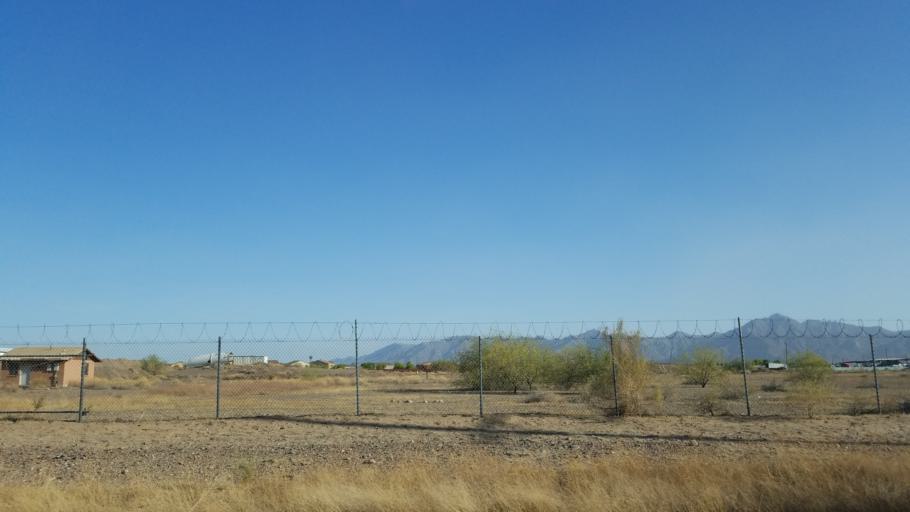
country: US
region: Arizona
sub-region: Maricopa County
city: Laveen
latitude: 33.3918
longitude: -112.2168
